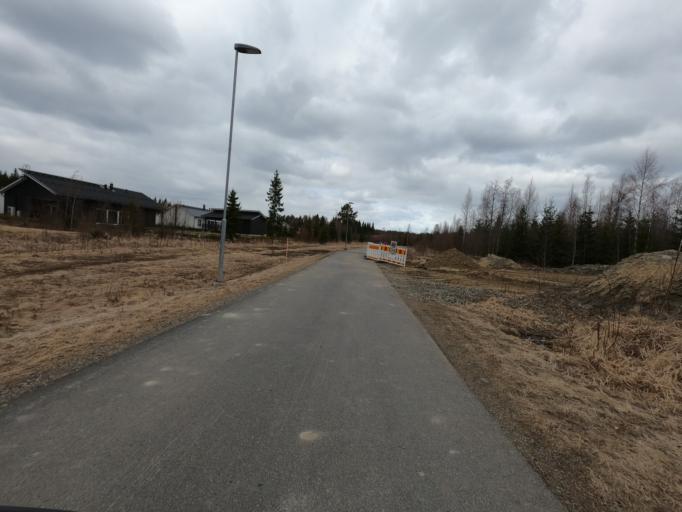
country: FI
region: North Karelia
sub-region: Joensuu
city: Joensuu
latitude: 62.5666
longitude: 29.8178
